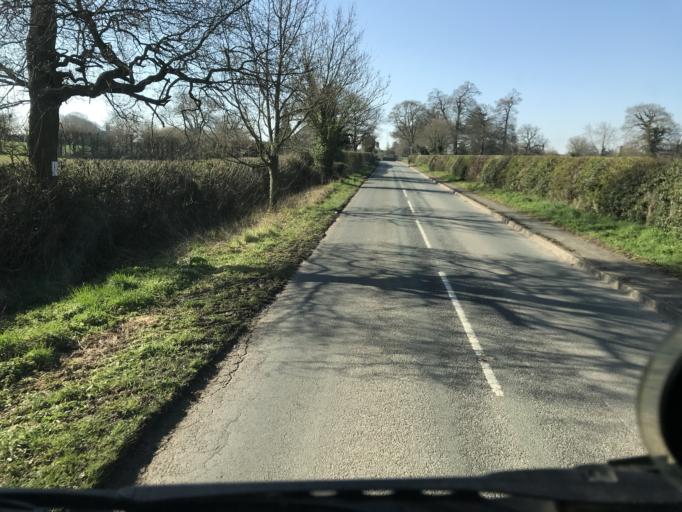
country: GB
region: England
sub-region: Cheshire West and Chester
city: Waverton
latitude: 53.1564
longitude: -2.8295
